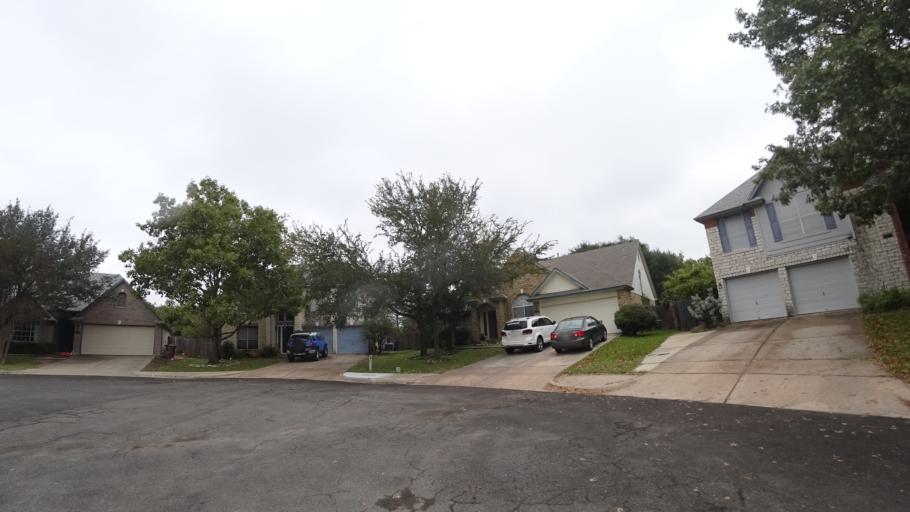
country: US
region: Texas
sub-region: Travis County
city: Shady Hollow
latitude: 30.1904
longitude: -97.8433
